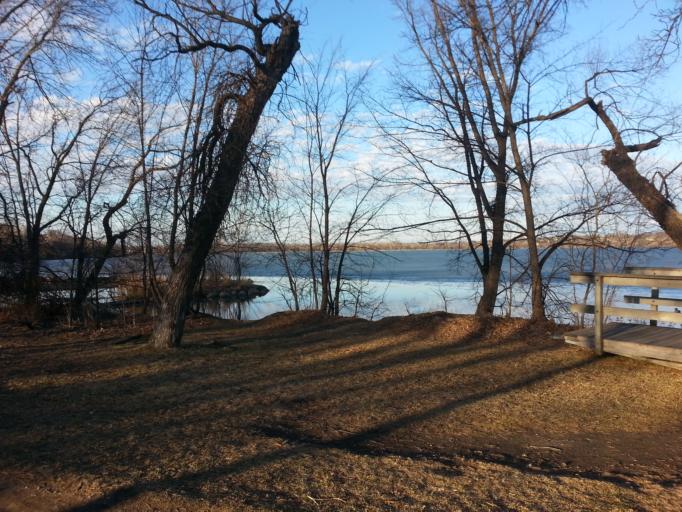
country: US
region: Minnesota
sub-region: Hennepin County
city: Saint Louis Park
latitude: 44.9179
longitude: -93.3136
